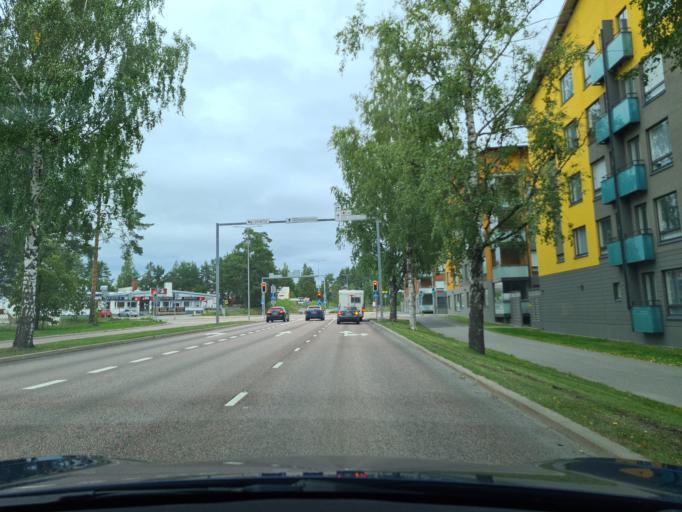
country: FI
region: South Karelia
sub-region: Lappeenranta
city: Lappeenranta
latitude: 61.0472
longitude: 28.1808
